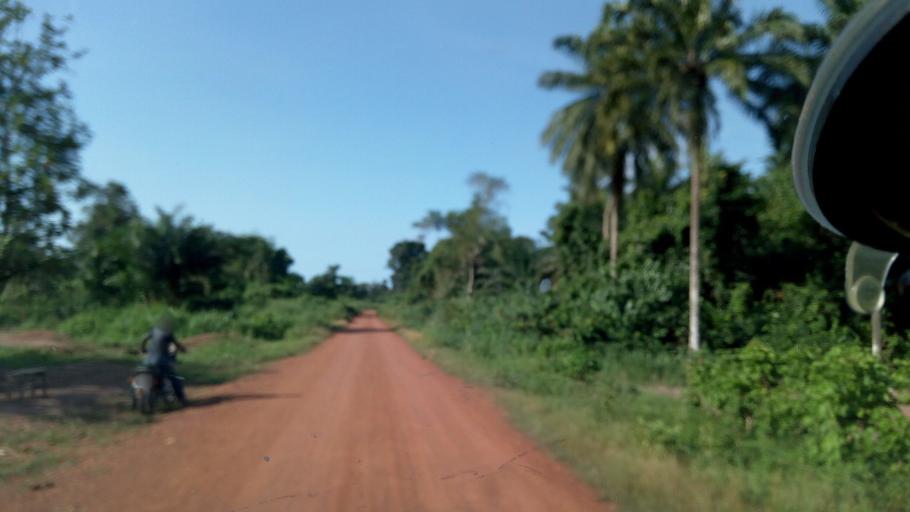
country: CD
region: Equateur
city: Libenge
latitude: 3.9340
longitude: 18.6986
